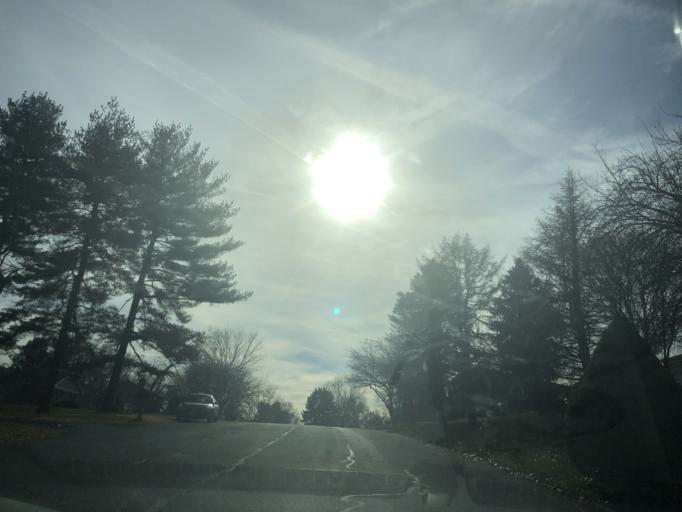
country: US
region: Maryland
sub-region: Howard County
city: Columbia
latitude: 39.2893
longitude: -76.8475
